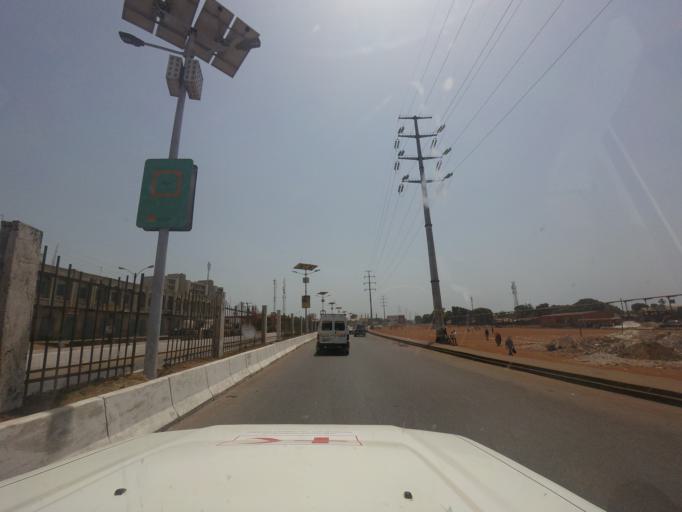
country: GN
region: Conakry
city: Conakry
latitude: 9.5494
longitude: -13.6613
